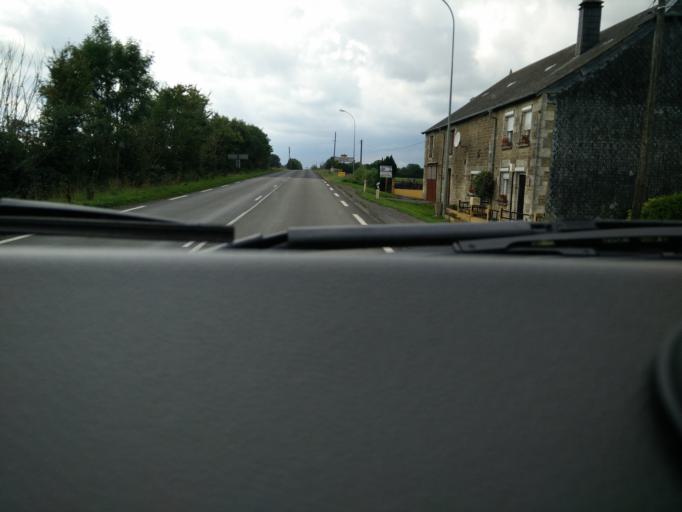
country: FR
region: Champagne-Ardenne
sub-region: Departement des Ardennes
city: Signy-le-Petit
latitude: 49.8724
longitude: 4.3653
